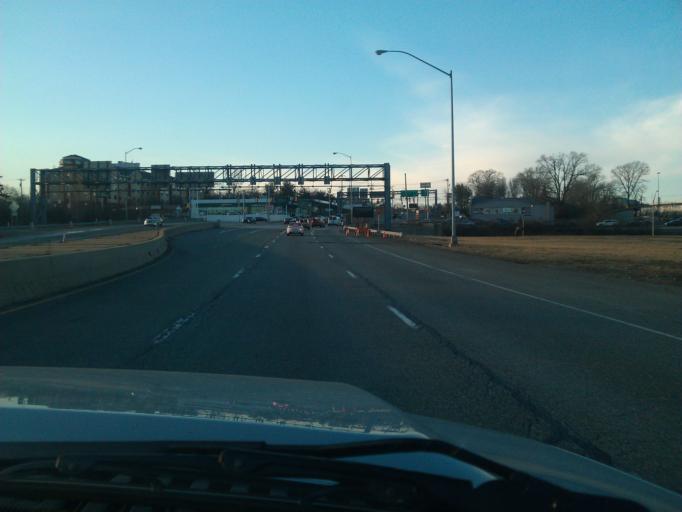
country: US
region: Pennsylvania
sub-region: Montgomery County
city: Plymouth Meeting
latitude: 40.1102
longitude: -75.2843
